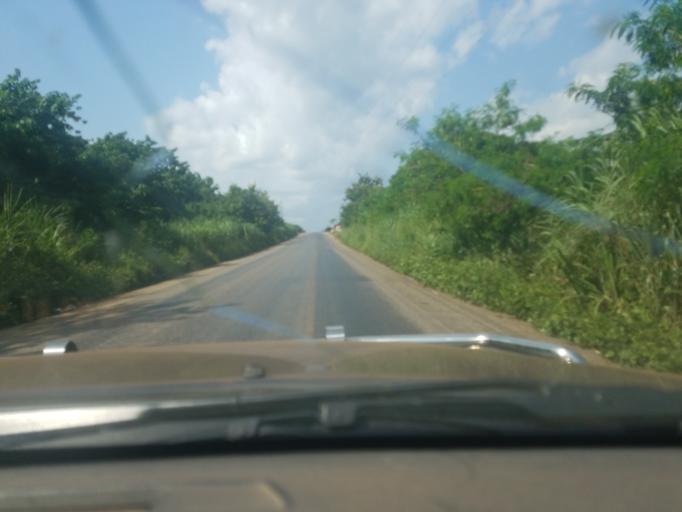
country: GH
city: Duayaw Nkwanta
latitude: 6.8825
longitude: -2.4209
